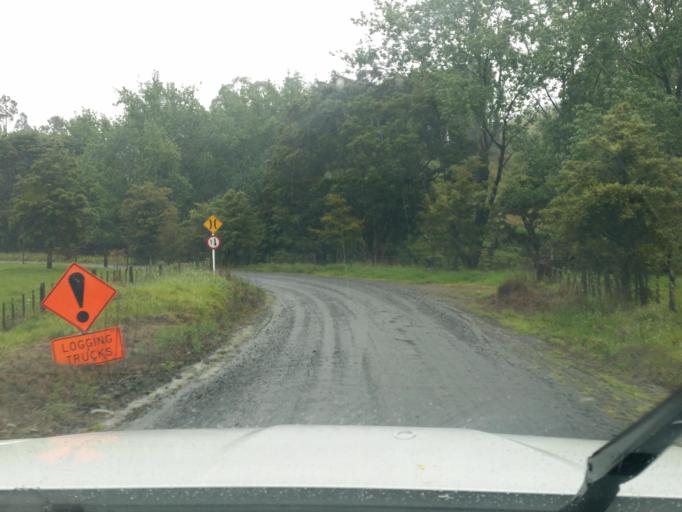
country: NZ
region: Northland
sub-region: Whangarei
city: Maungatapere
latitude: -35.8111
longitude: 174.0375
